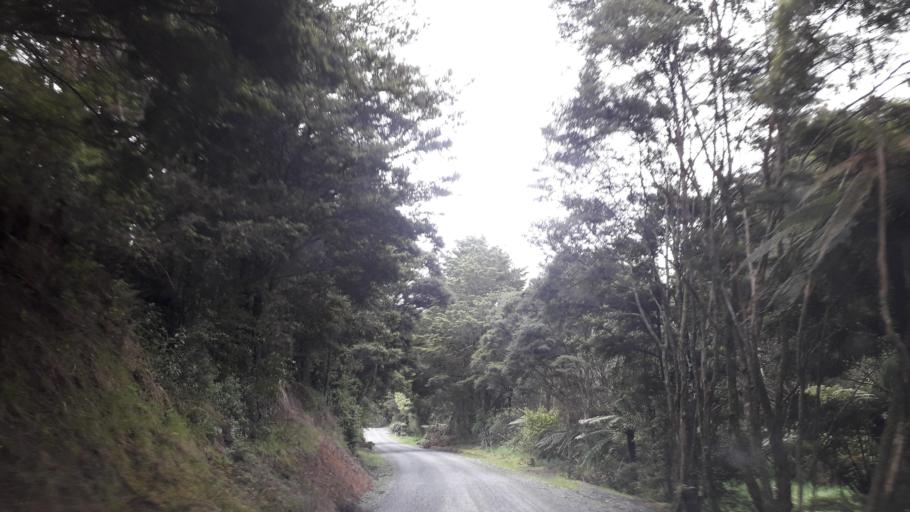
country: NZ
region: Northland
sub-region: Far North District
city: Taipa
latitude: -35.0681
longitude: 173.5527
